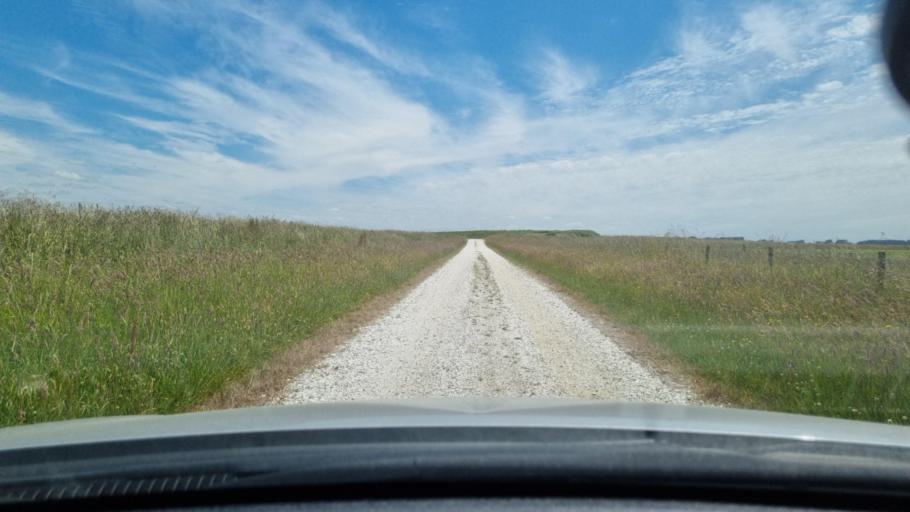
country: NZ
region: Southland
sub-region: Invercargill City
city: Invercargill
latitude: -46.3874
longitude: 168.2583
